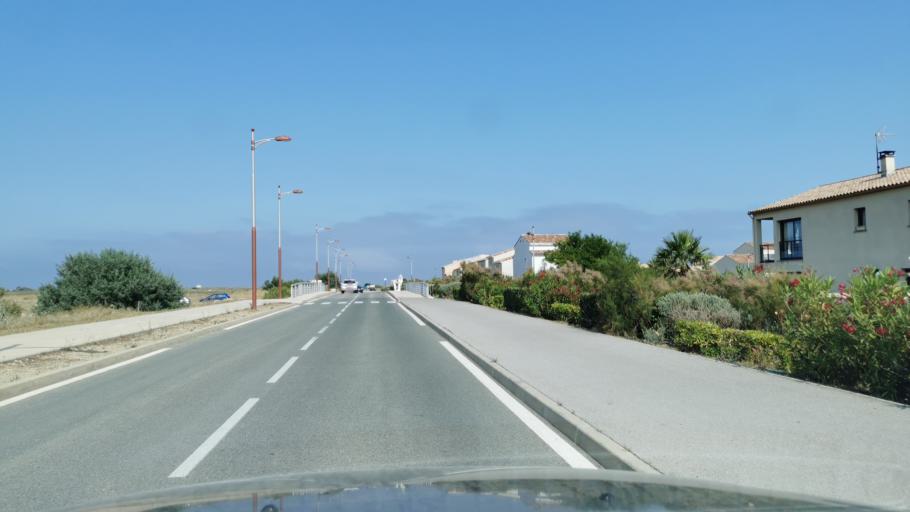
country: FR
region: Languedoc-Roussillon
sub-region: Departement de l'Aude
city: Gruissan
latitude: 43.1171
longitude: 3.1175
